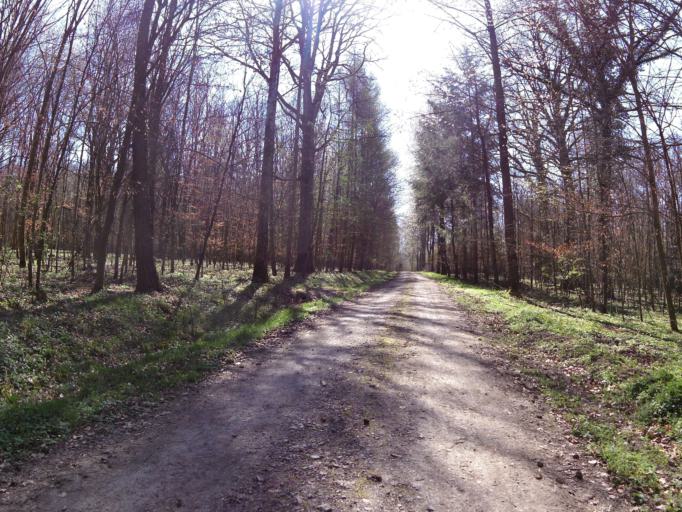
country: DE
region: Bavaria
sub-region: Regierungsbezirk Unterfranken
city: Rottendorf
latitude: 49.8203
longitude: 10.0479
